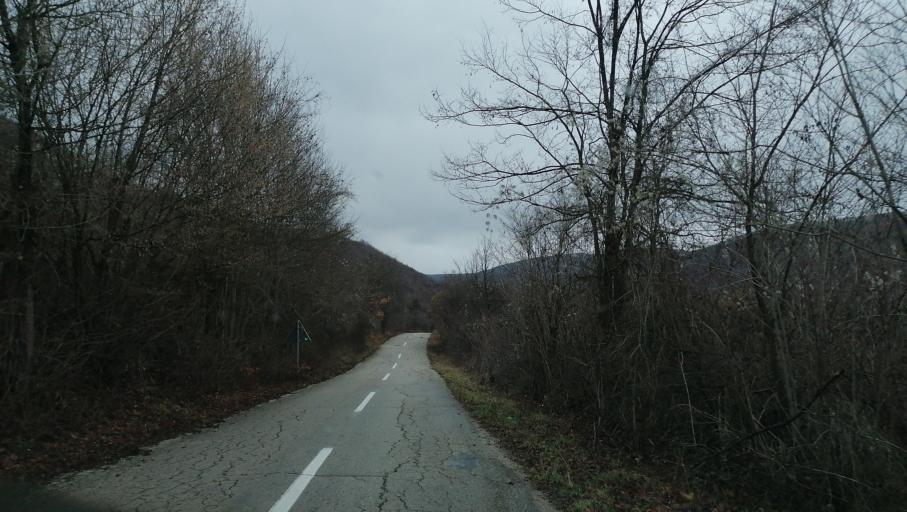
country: RS
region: Central Serbia
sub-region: Pirotski Okrug
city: Dimitrovgrad
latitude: 42.9577
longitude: 22.7826
